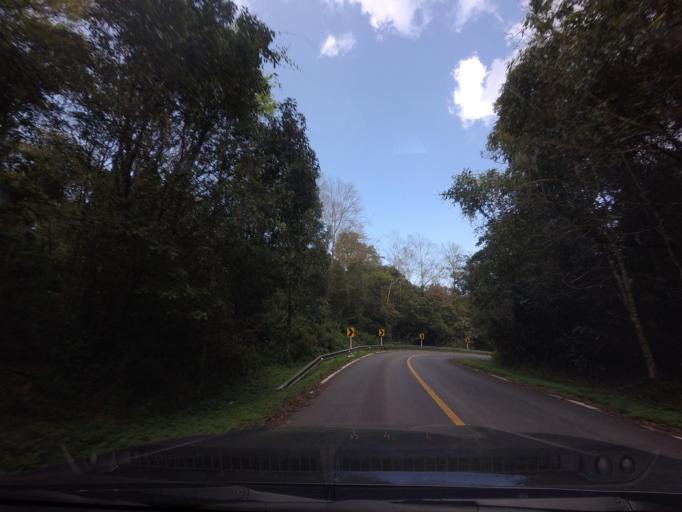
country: TH
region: Phetchabun
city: Lom Kao
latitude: 16.9536
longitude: 101.0278
